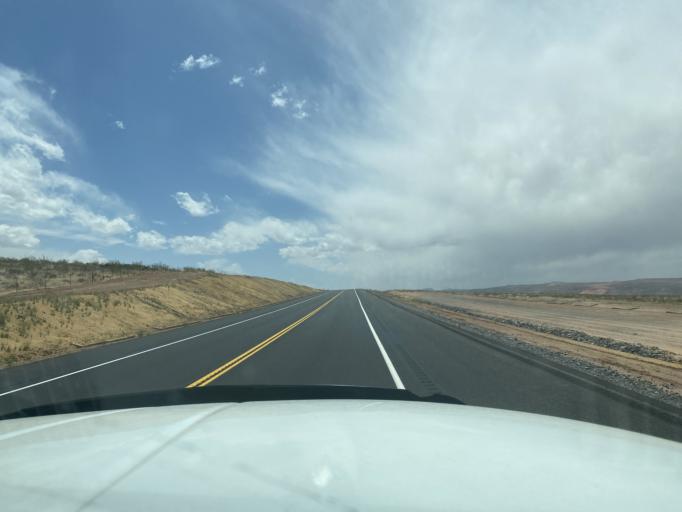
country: US
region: Utah
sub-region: Washington County
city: Hurricane
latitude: 37.1612
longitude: -113.3459
